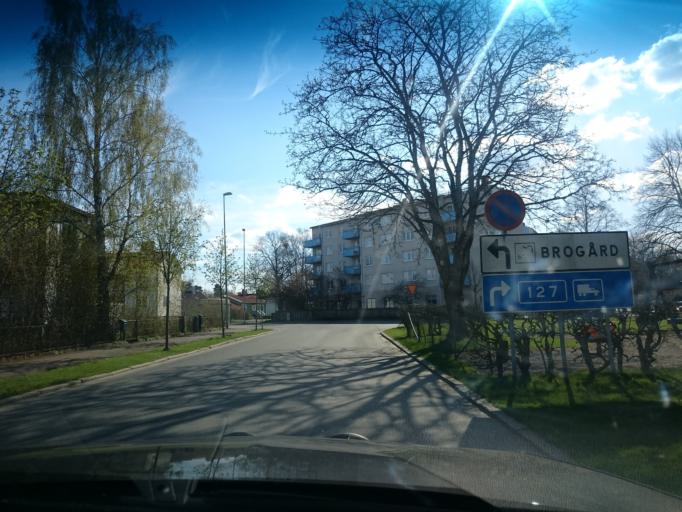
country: SE
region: Joenkoeping
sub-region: Vetlanda Kommun
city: Vetlanda
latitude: 57.4274
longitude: 15.0707
